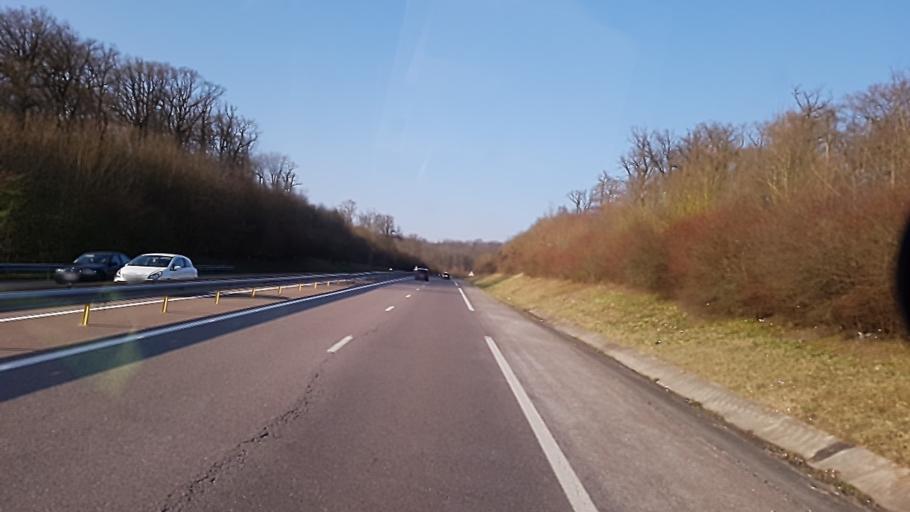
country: DE
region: Saarland
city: Kleinblittersdorf
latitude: 49.1250
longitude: 7.0349
